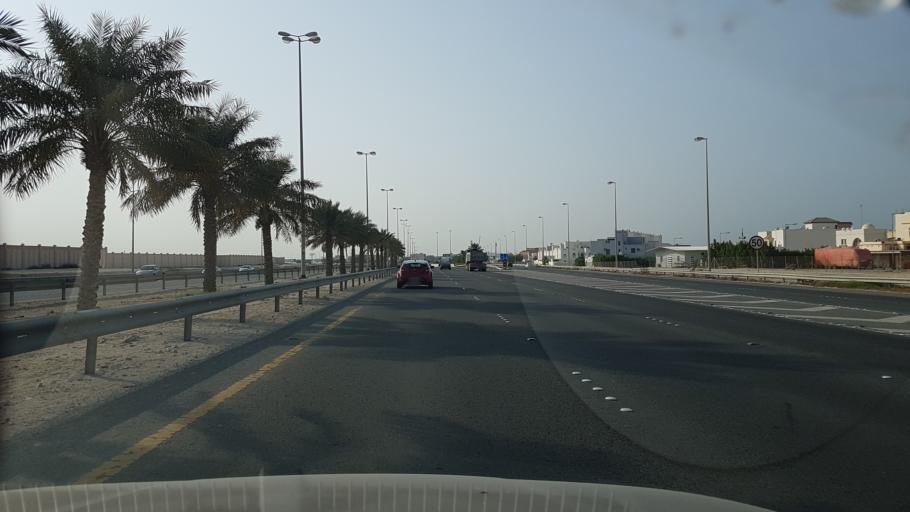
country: BH
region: Central Governorate
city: Madinat Hamad
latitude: 26.1045
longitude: 50.5112
